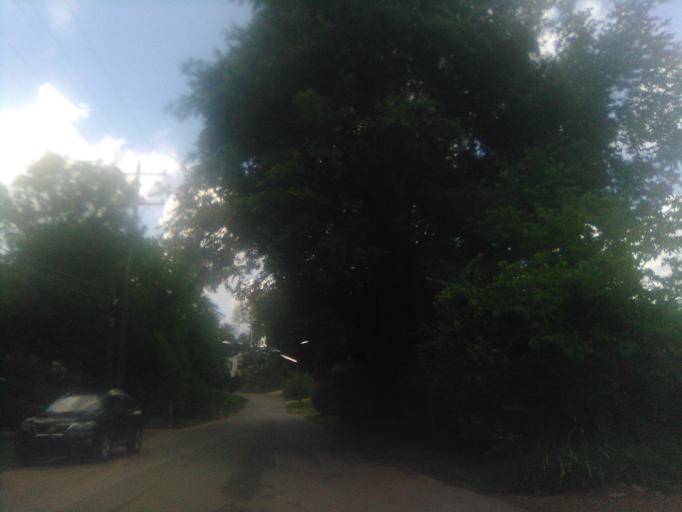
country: US
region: Tennessee
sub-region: Davidson County
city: Belle Meade
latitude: 36.1114
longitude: -86.8282
